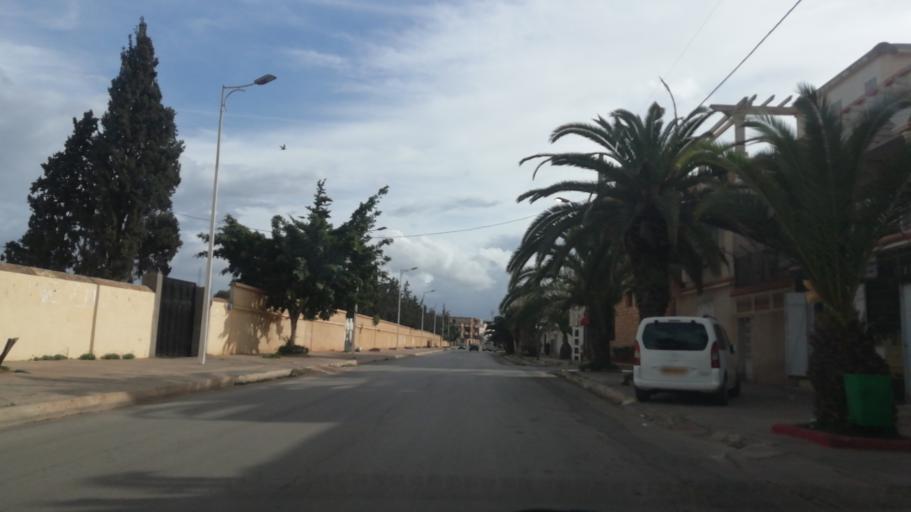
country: DZ
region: Oran
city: Es Senia
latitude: 35.6642
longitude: -0.6396
